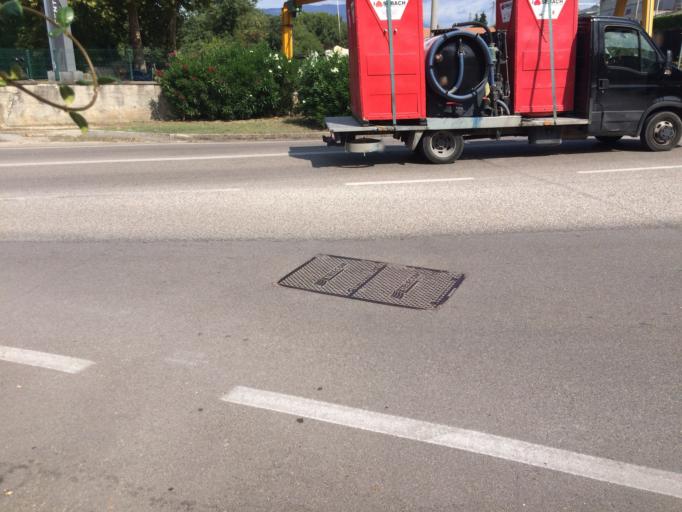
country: IT
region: Veneto
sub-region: Provincia di Verona
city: Volargne
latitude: 45.5220
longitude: 10.8063
